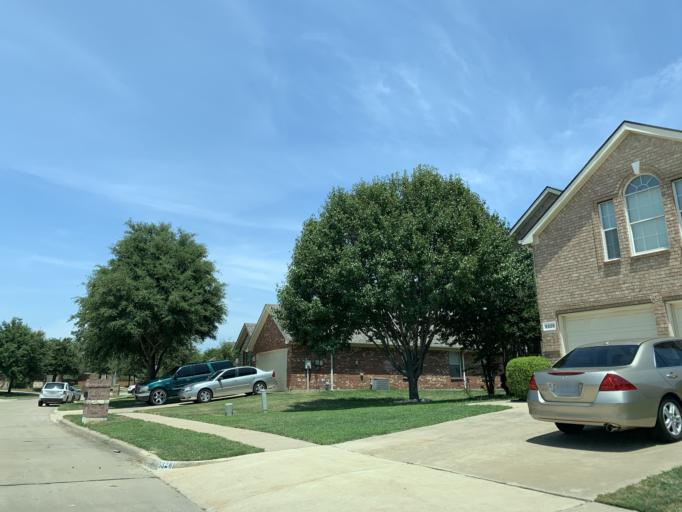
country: US
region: Texas
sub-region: Dallas County
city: Cedar Hill
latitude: 32.6439
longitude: -97.0217
